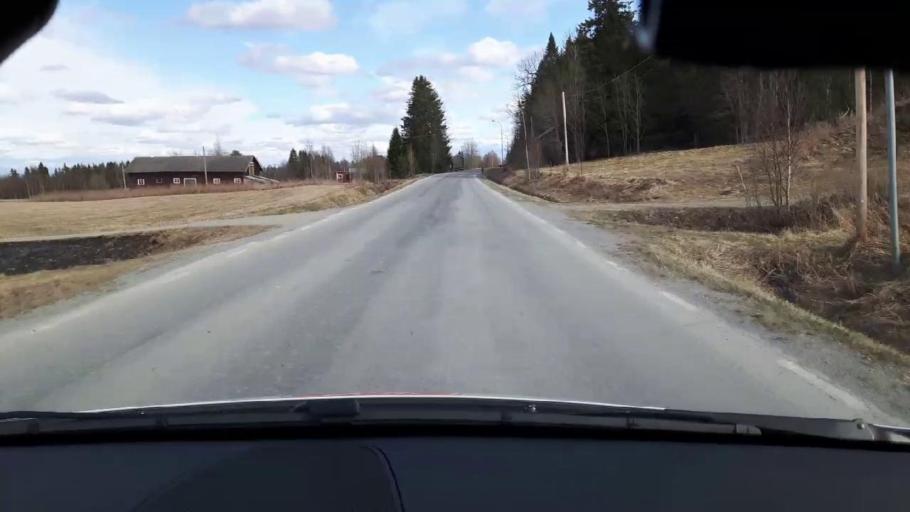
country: SE
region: Jaemtland
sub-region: Bergs Kommun
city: Hoverberg
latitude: 62.7847
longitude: 14.5009
